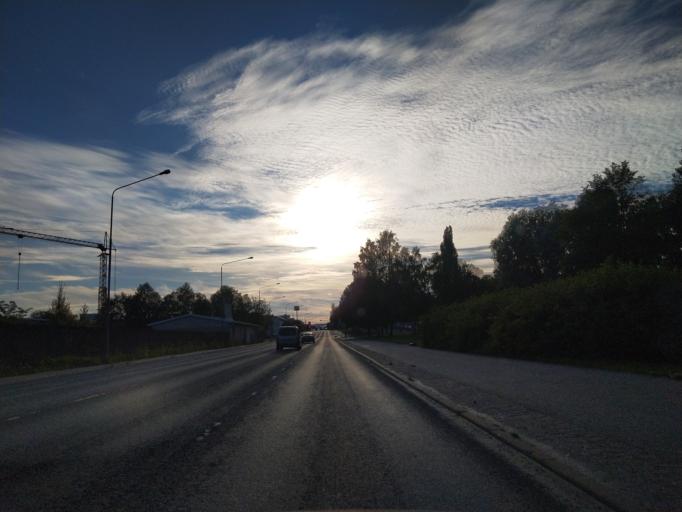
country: FI
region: Varsinais-Suomi
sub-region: Turku
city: Turku
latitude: 60.4494
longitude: 22.3144
